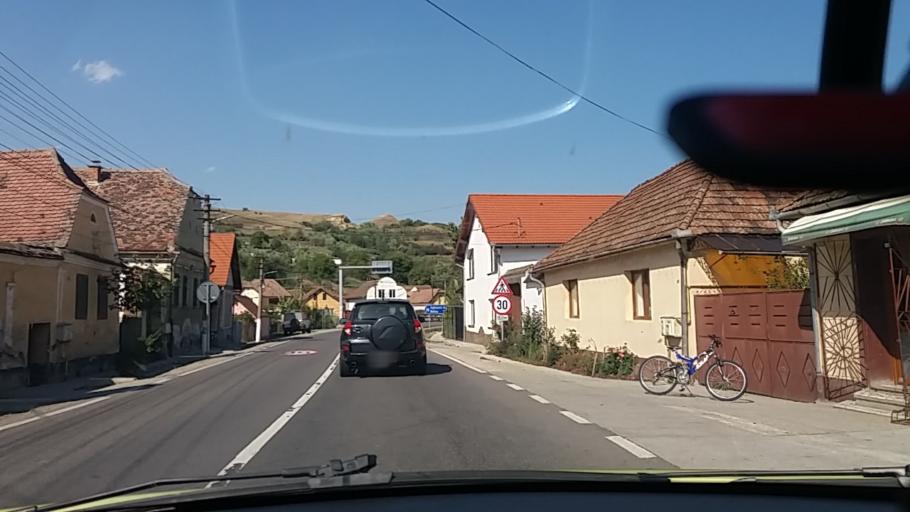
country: RO
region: Sibiu
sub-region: Comuna Slimnic
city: Slimnic
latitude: 45.9193
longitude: 24.1553
